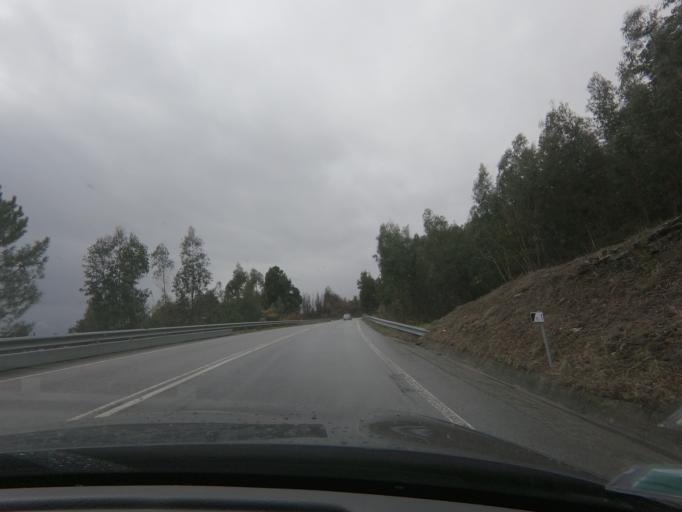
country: PT
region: Braga
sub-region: Celorico de Basto
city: Celorico de Basto
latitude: 41.3494
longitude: -8.0180
